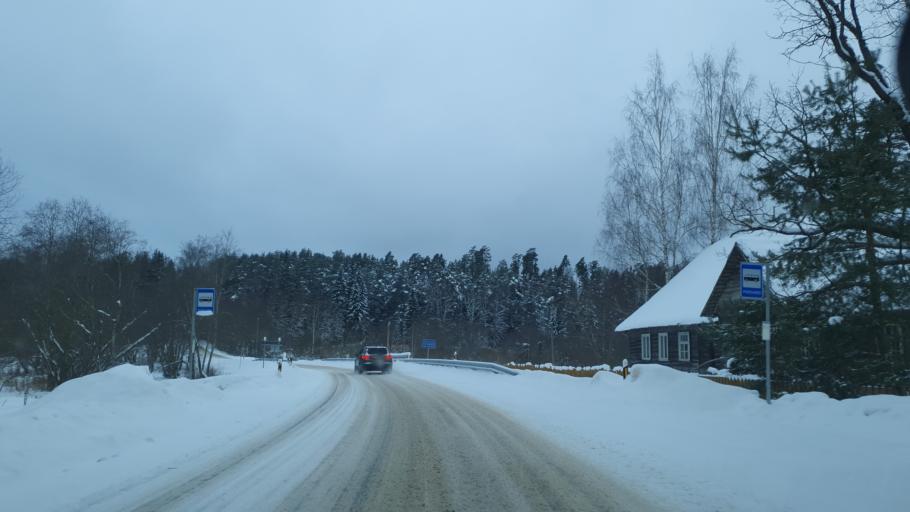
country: EE
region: Polvamaa
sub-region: Polva linn
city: Polva
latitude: 58.1154
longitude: 27.0876
